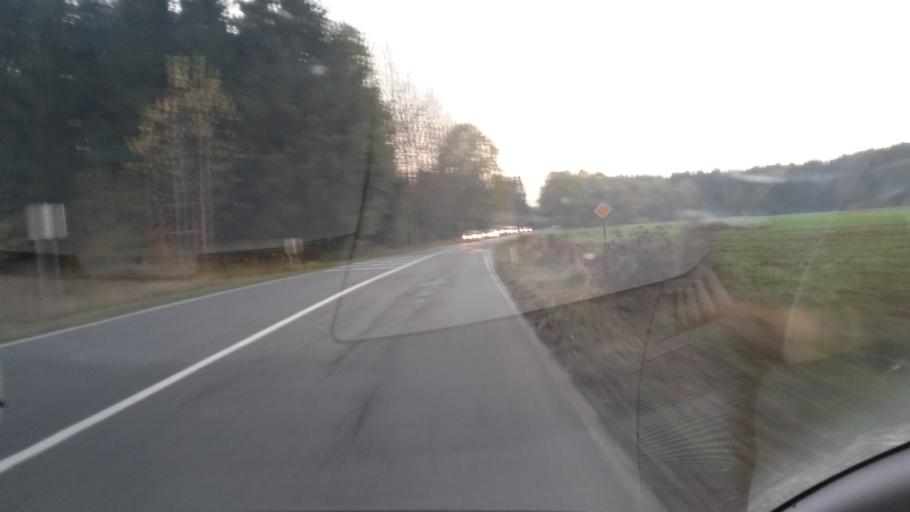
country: BE
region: Wallonia
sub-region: Province du Luxembourg
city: Etalle
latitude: 49.6638
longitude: 5.5966
